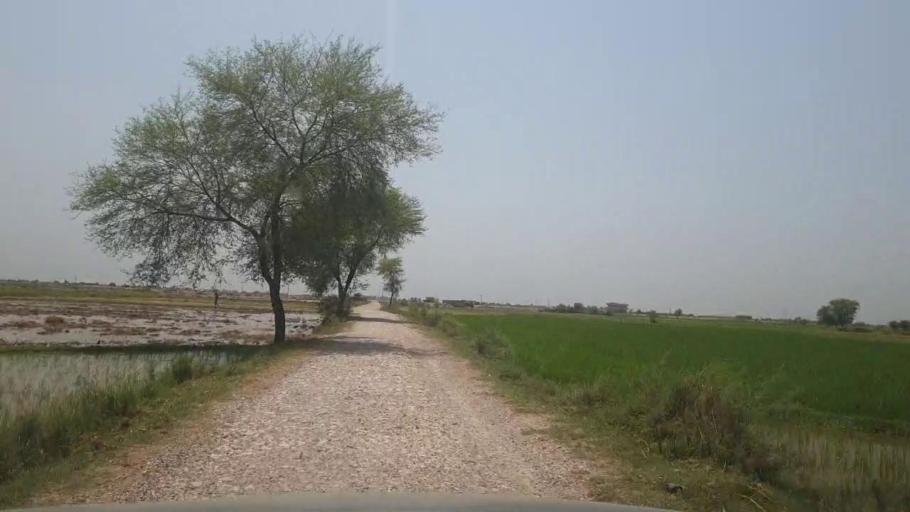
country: PK
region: Sindh
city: Lakhi
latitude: 27.8434
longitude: 68.6631
